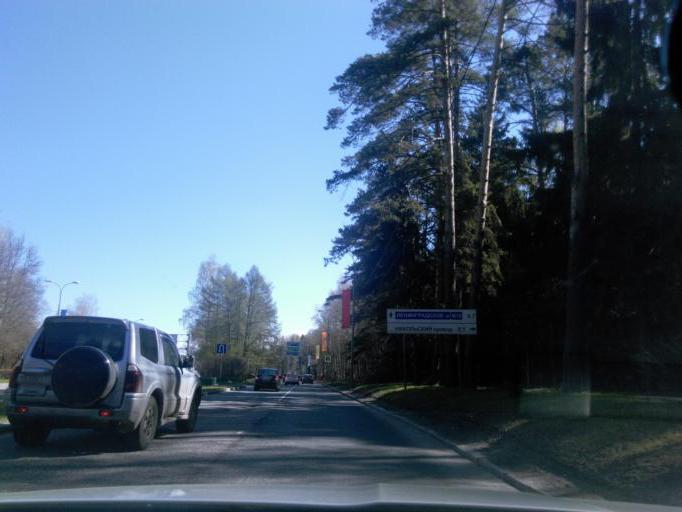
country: RU
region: Moskovskaya
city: Rzhavki
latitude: 55.9962
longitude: 37.2349
